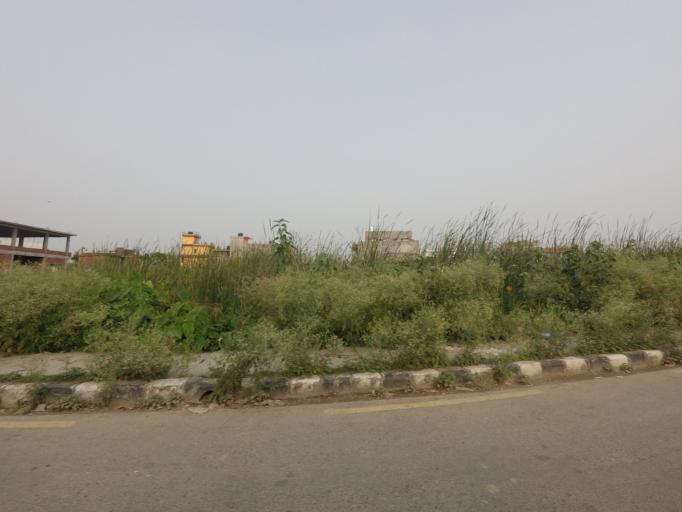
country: NP
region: Western Region
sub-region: Lumbini Zone
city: Bhairahawa
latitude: 27.5107
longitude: 83.4433
